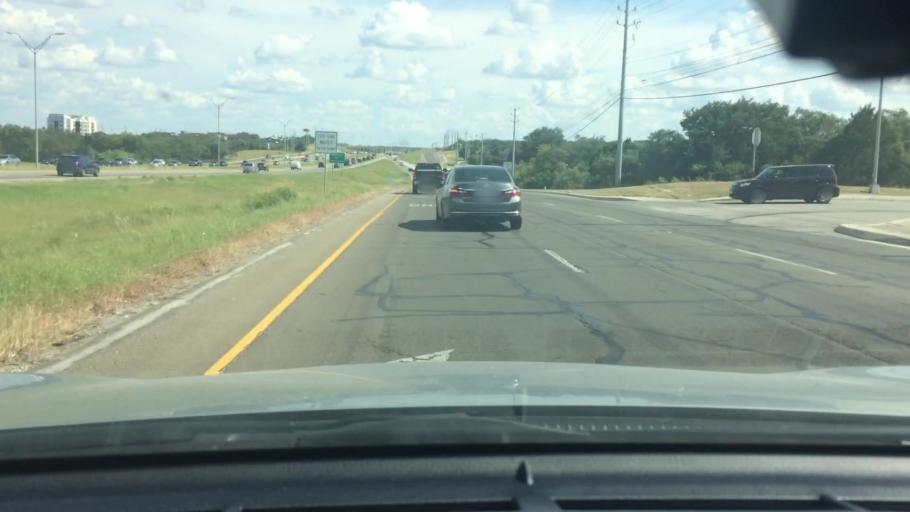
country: US
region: Texas
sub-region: Bexar County
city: Leon Valley
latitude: 29.4704
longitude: -98.6960
